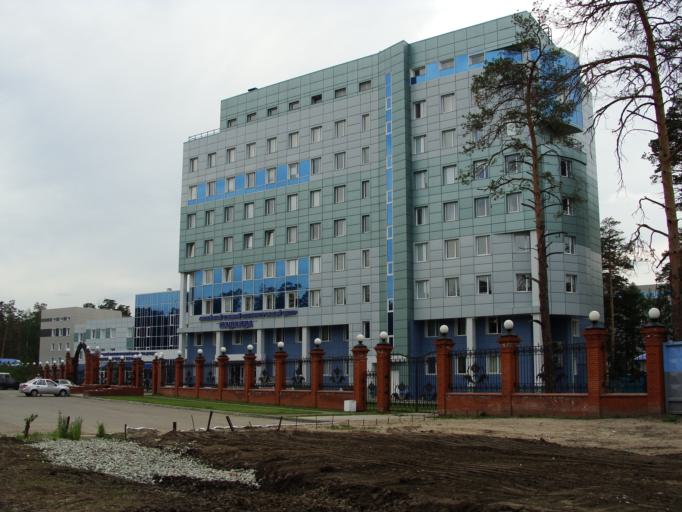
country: RU
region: Altai Krai
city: Zaton
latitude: 53.2814
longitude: 83.7488
